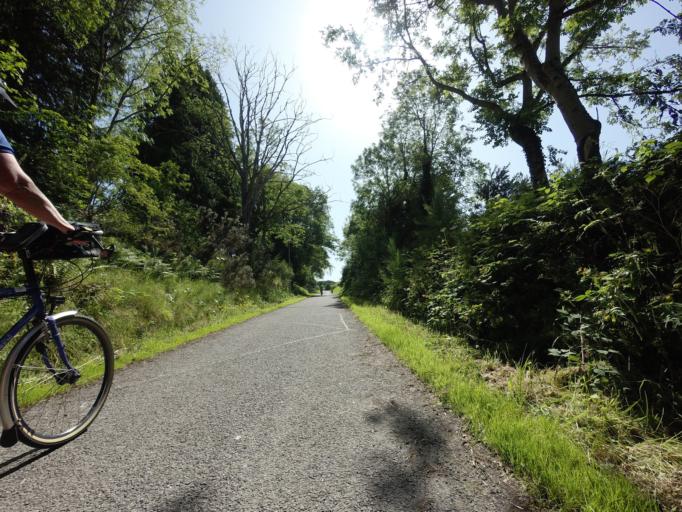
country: GB
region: Scotland
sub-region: Highland
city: Inverness
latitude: 57.4758
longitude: -4.1603
